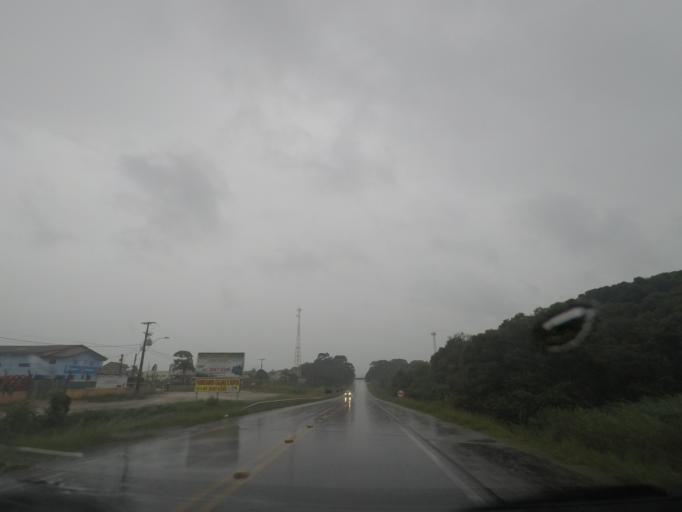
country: BR
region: Parana
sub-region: Almirante Tamandare
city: Almirante Tamandare
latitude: -25.3536
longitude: -49.2975
